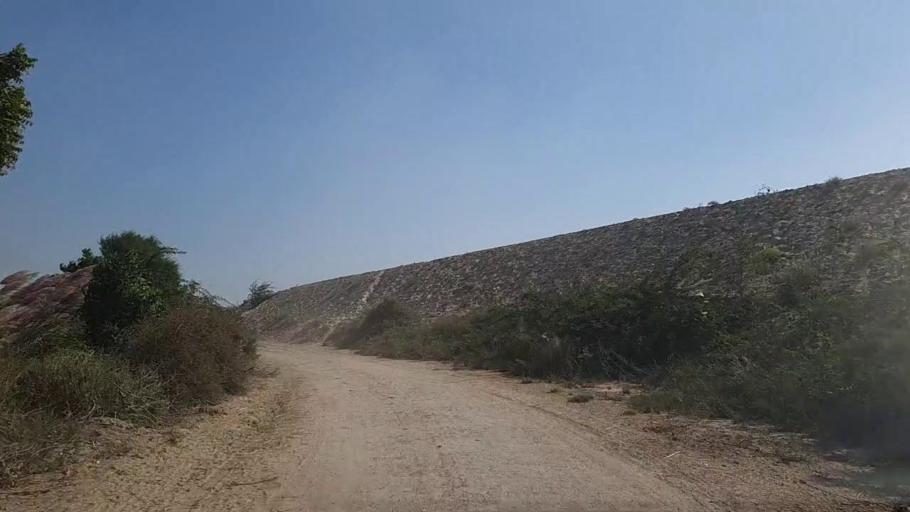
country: PK
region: Sindh
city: Daro Mehar
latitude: 24.8121
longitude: 68.0738
